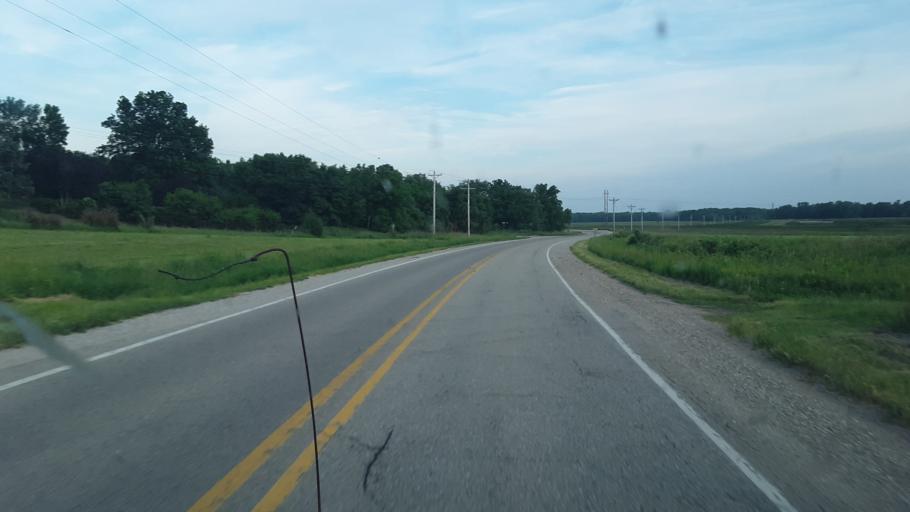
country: US
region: Iowa
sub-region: Benton County
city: Belle Plaine
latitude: 41.9461
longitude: -92.4164
